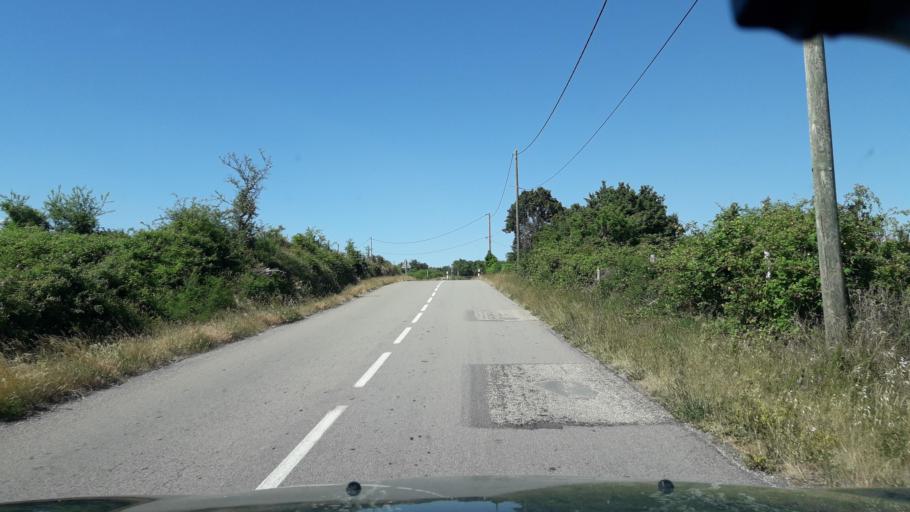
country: FR
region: Rhone-Alpes
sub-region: Departement de l'Ardeche
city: Villeneuve-de-Berg
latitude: 44.6240
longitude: 4.5500
